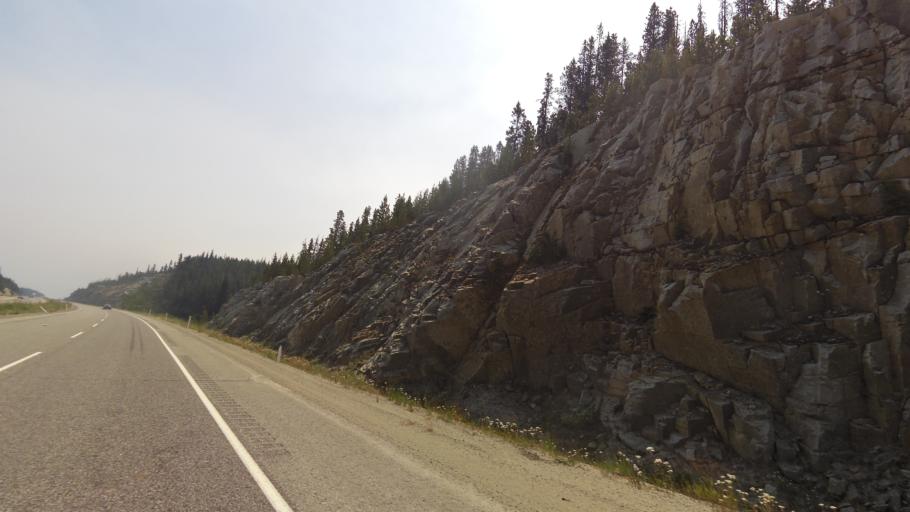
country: CA
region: British Columbia
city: Peachland
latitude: 49.8951
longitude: -119.9737
